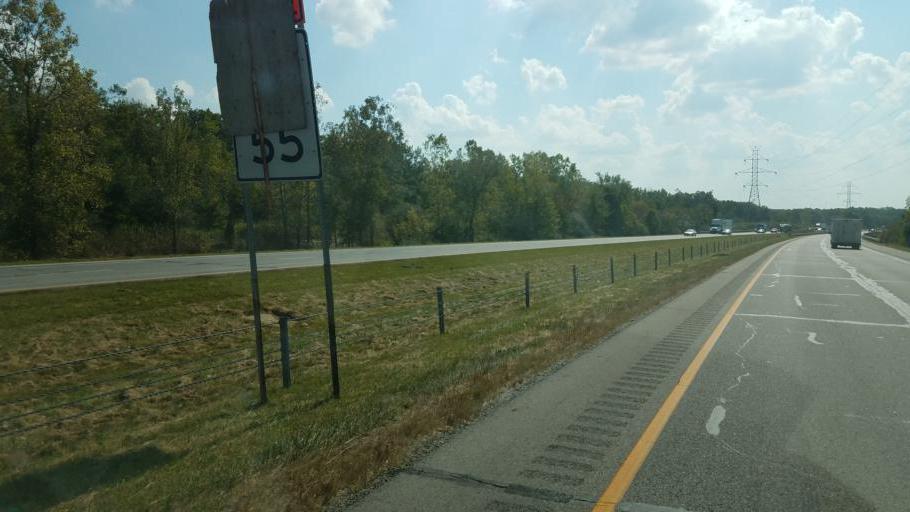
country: US
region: Indiana
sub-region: Allen County
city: Huntertown
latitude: 41.2395
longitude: -85.0931
